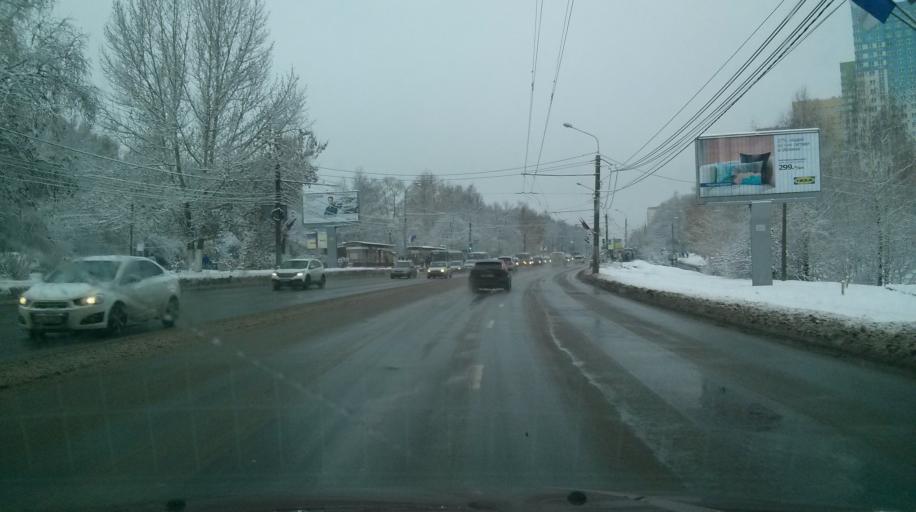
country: RU
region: Nizjnij Novgorod
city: Nizhniy Novgorod
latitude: 56.2413
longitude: 43.9630
